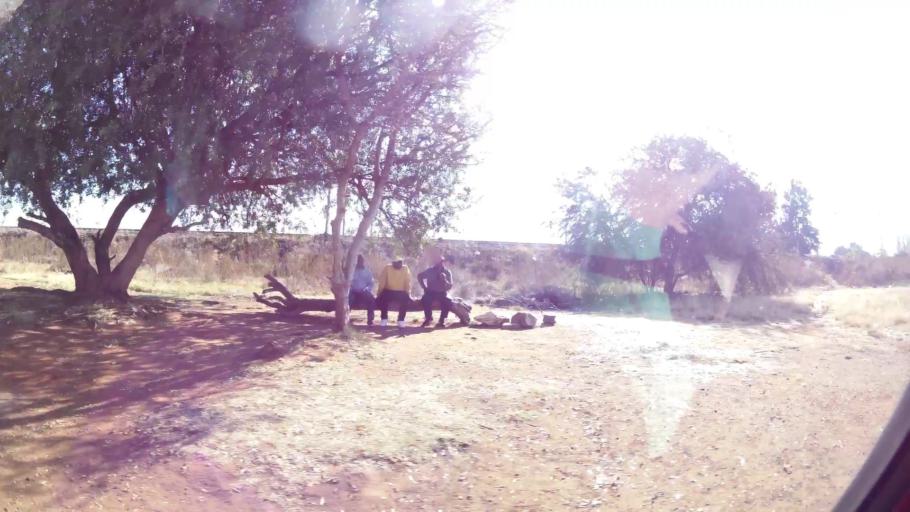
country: ZA
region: Gauteng
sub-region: City of Johannesburg Metropolitan Municipality
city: Soweto
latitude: -26.2366
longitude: 27.8731
